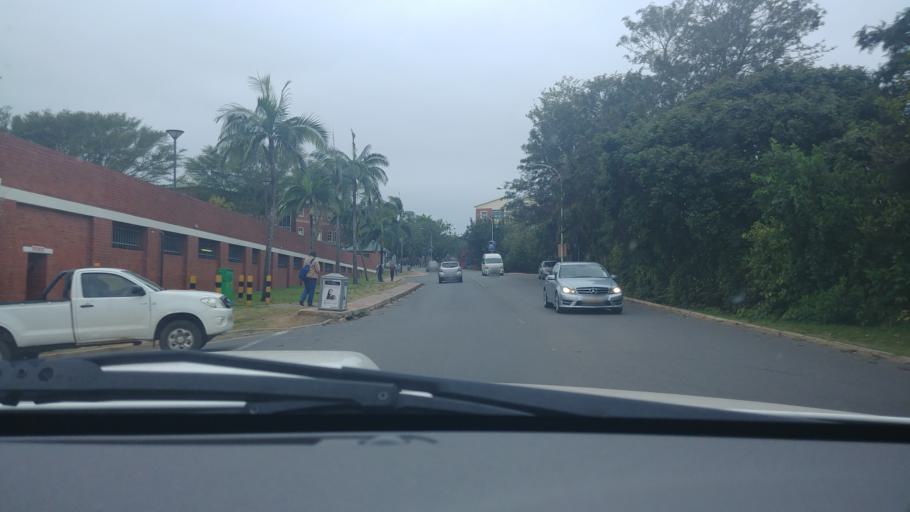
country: ZA
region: KwaZulu-Natal
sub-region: eThekwini Metropolitan Municipality
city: Durban
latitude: -29.7149
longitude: 31.0523
